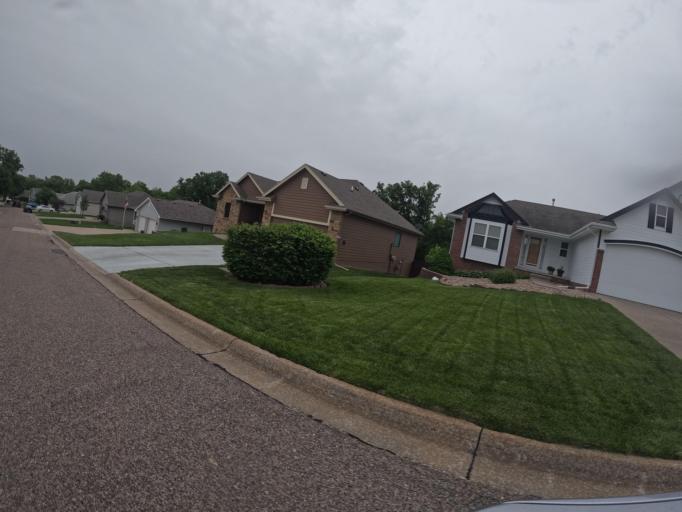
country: US
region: Nebraska
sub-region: Sarpy County
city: Offutt Air Force Base
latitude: 41.0460
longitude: -95.9748
